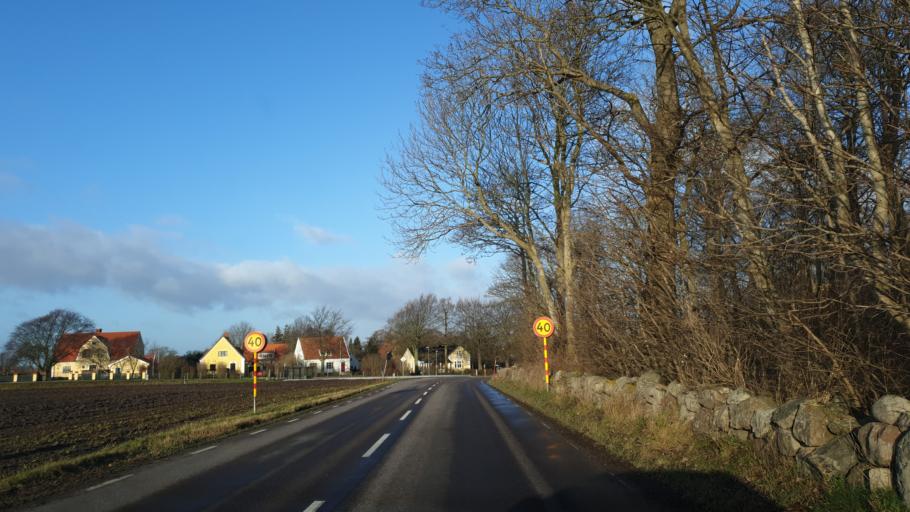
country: SE
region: Skane
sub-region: Vellinge Kommun
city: Vellinge
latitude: 55.4986
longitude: 13.0285
